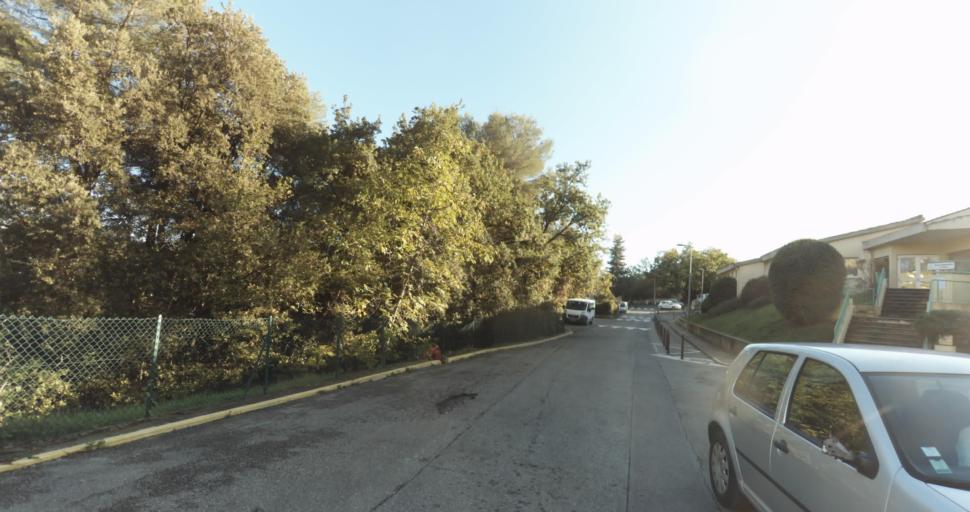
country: FR
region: Provence-Alpes-Cote d'Azur
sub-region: Departement des Alpes-Maritimes
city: Vence
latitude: 43.7270
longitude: 7.1236
